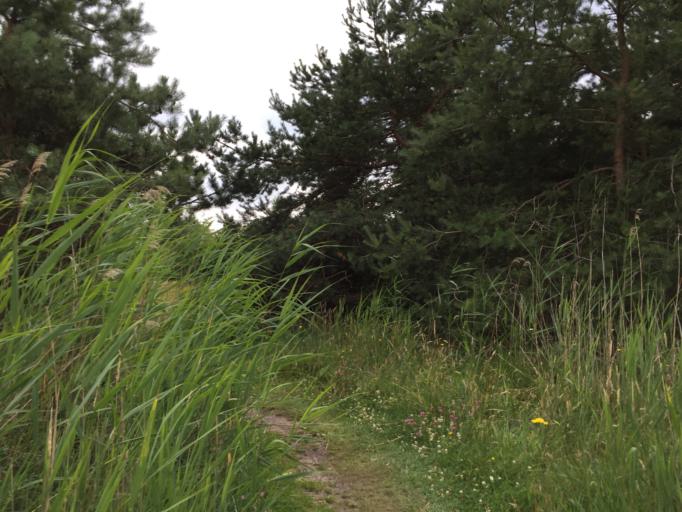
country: DE
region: Mecklenburg-Vorpommern
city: Hiddensee
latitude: 54.4923
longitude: 13.0696
